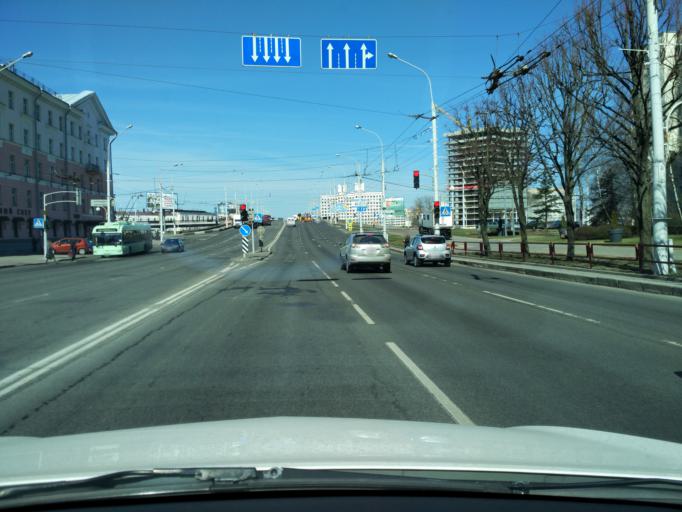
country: BY
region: Minsk
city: Minsk
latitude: 53.8810
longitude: 27.5358
